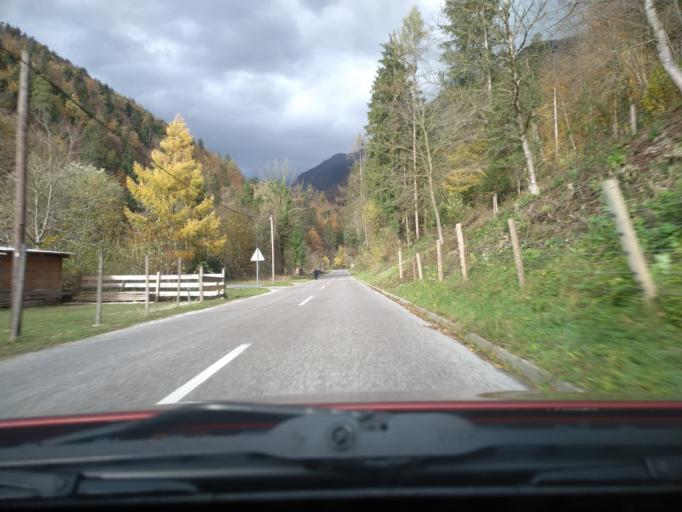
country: SI
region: Kamnik
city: Mekinje
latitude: 46.2813
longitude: 14.6152
